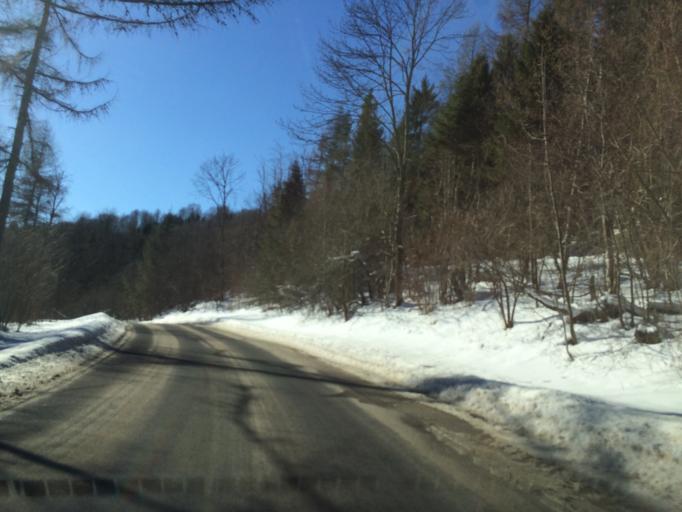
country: PL
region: Subcarpathian Voivodeship
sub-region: Powiat bieszczadzki
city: Lutowiska
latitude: 49.1297
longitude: 22.6673
